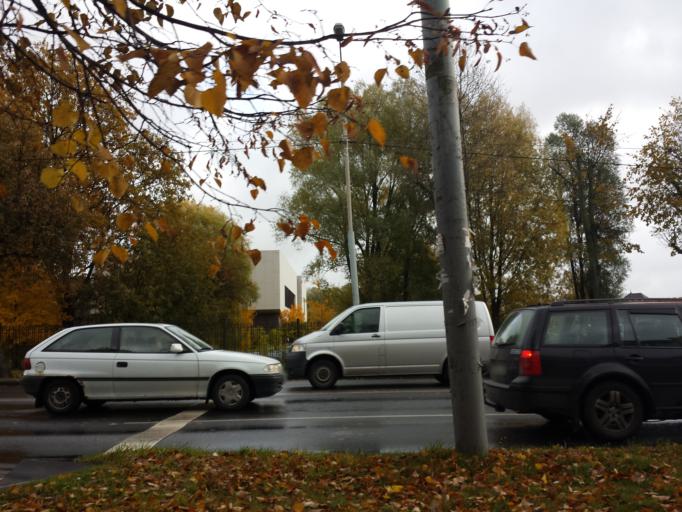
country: RU
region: Kaliningrad
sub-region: Gorod Kaliningrad
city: Kaliningrad
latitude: 54.7243
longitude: 20.5258
